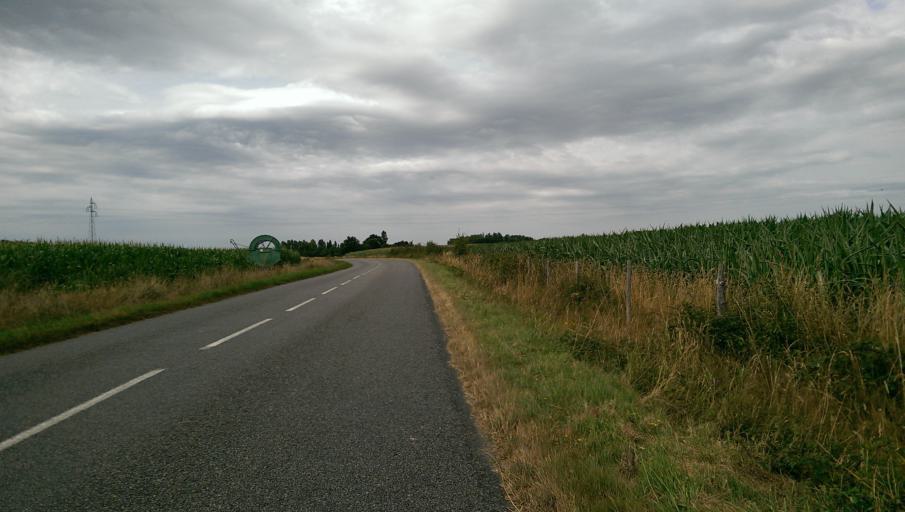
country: FR
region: Pays de la Loire
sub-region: Departement de la Loire-Atlantique
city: Vieillevigne
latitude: 46.9857
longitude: -1.4297
